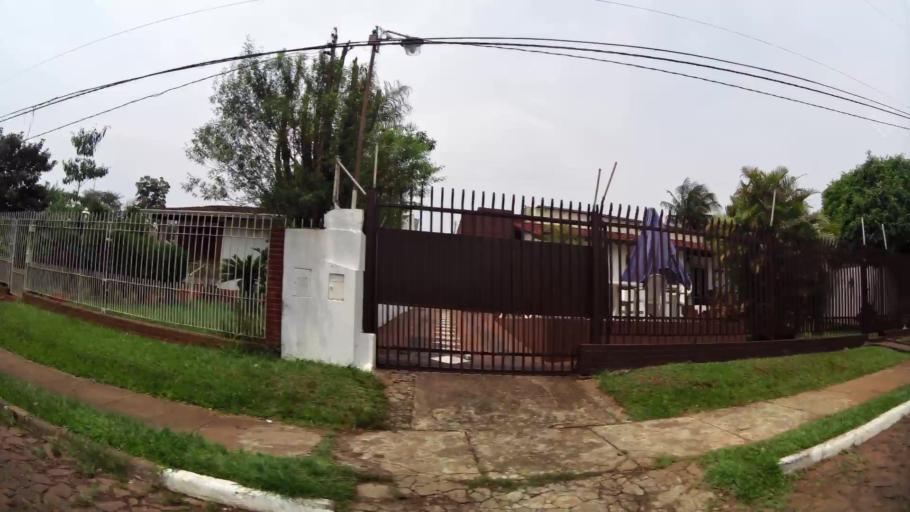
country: PY
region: Alto Parana
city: Presidente Franco
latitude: -25.5504
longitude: -54.6195
